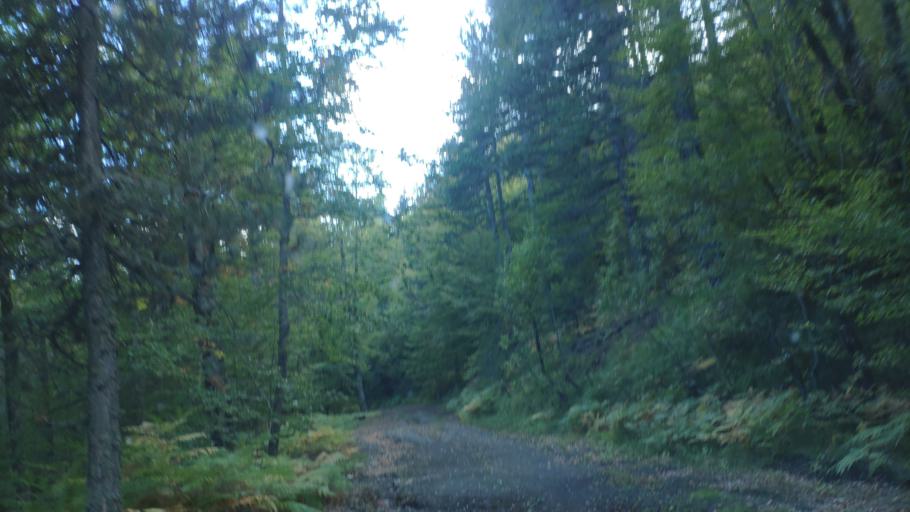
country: AL
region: Korce
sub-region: Rrethi i Devollit
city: Miras
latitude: 40.3463
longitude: 20.8994
